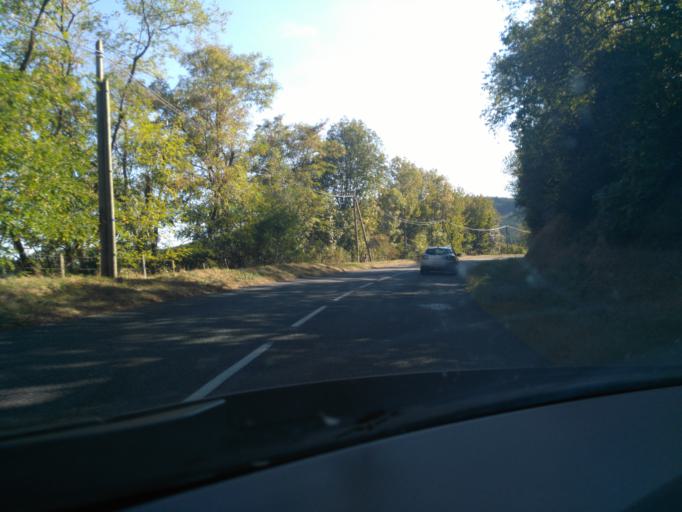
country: FR
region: Rhone-Alpes
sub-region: Departement du Rhone
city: Tarare
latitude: 45.8750
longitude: 4.4196
